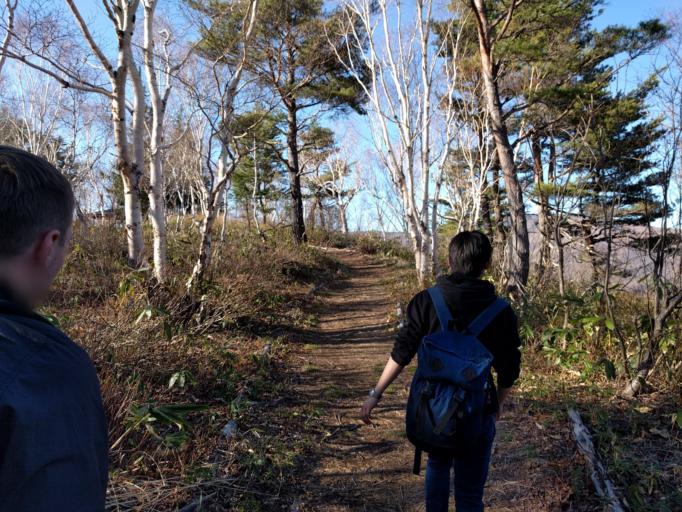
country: JP
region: Nagano
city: Nakano
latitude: 36.7235
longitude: 138.4782
